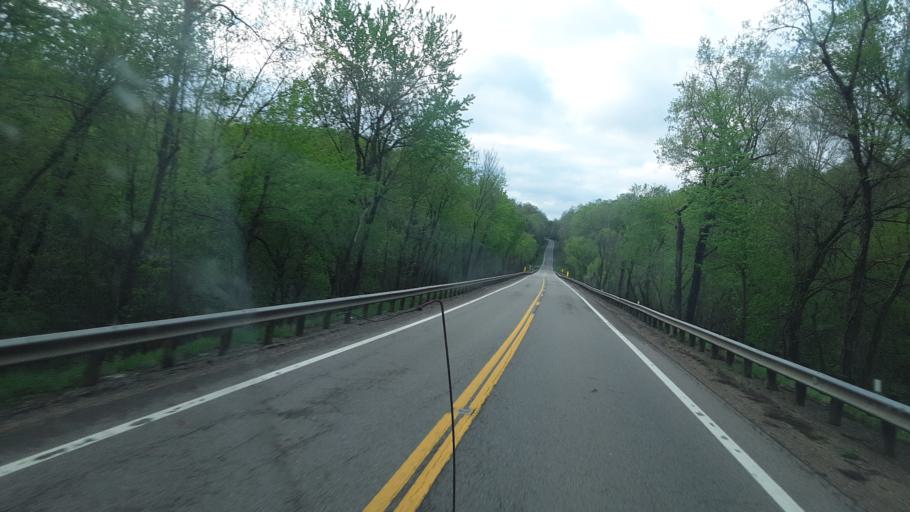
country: US
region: Ohio
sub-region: Coshocton County
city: West Lafayette
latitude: 40.1486
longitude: -81.7997
